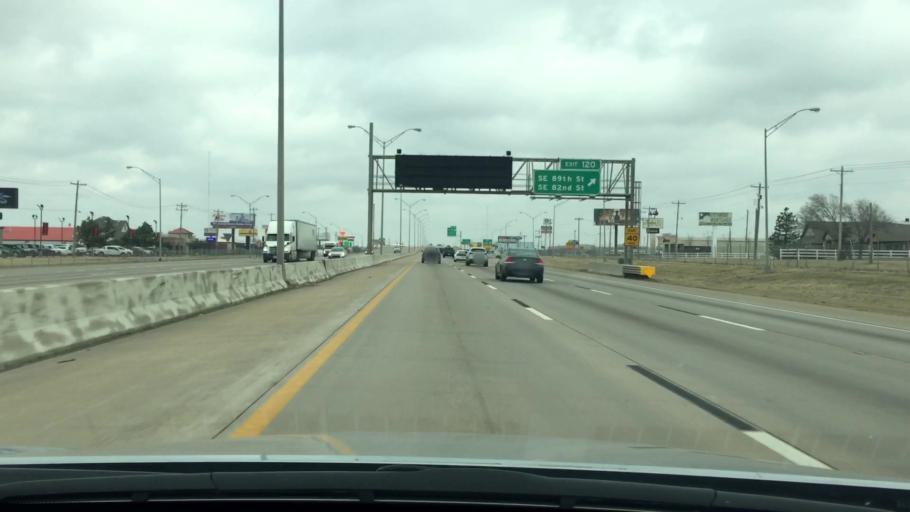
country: US
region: Oklahoma
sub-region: Cleveland County
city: Moore
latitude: 35.3726
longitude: -97.4949
